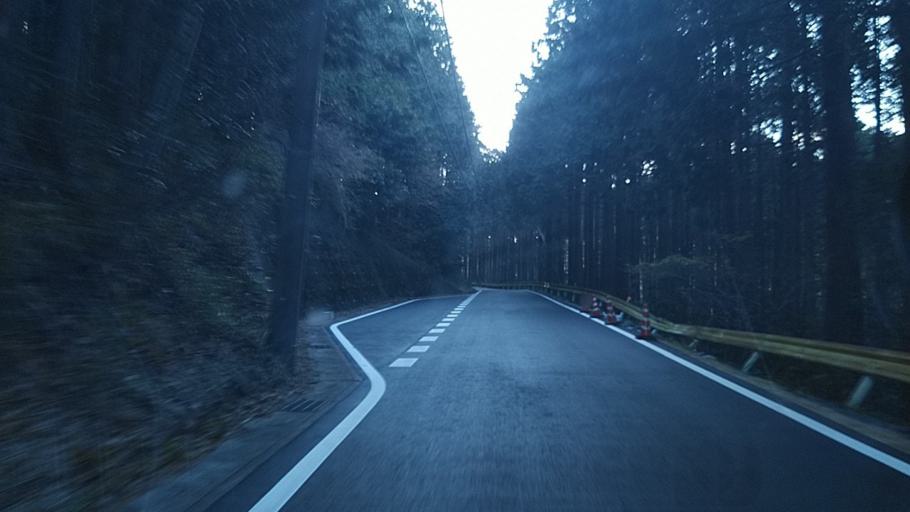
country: JP
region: Chiba
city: Kimitsu
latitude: 35.2554
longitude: 139.9506
